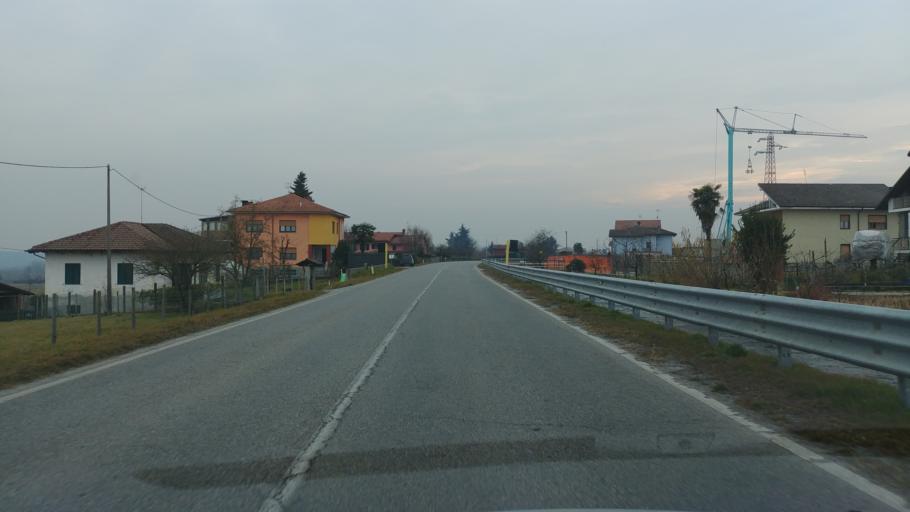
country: IT
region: Piedmont
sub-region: Provincia di Cuneo
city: Sant'Albano Stura
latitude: 44.5244
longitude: 7.7037
